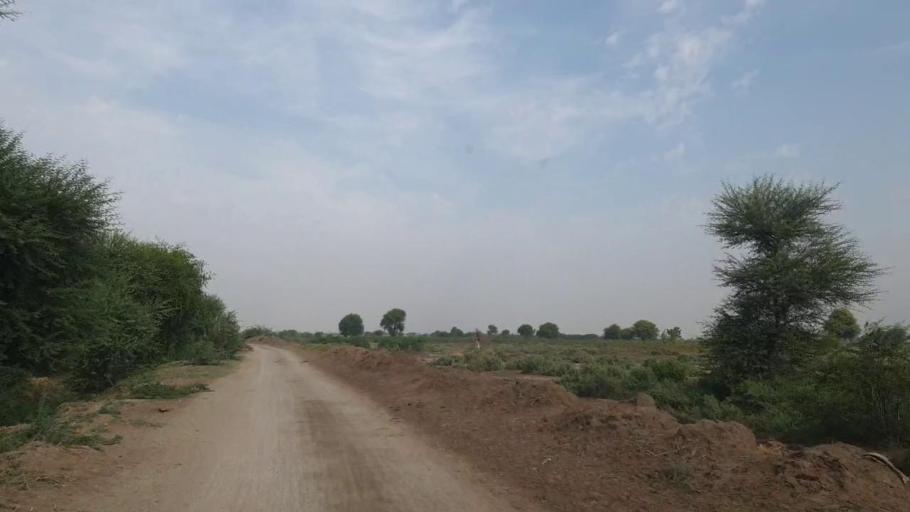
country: PK
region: Sindh
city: Rajo Khanani
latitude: 24.9689
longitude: 68.9968
